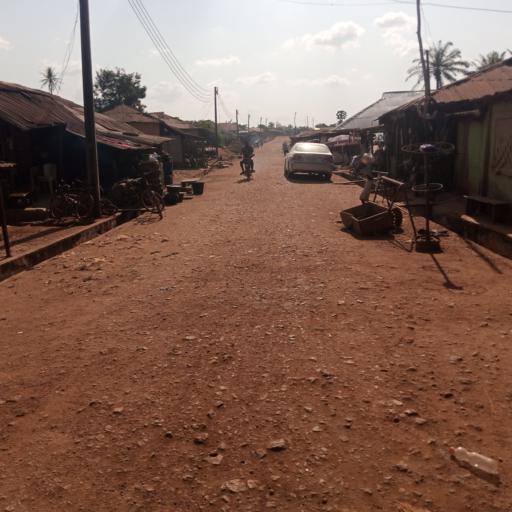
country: NG
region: Osun
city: Modakeke
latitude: 7.1726
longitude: 4.3605
